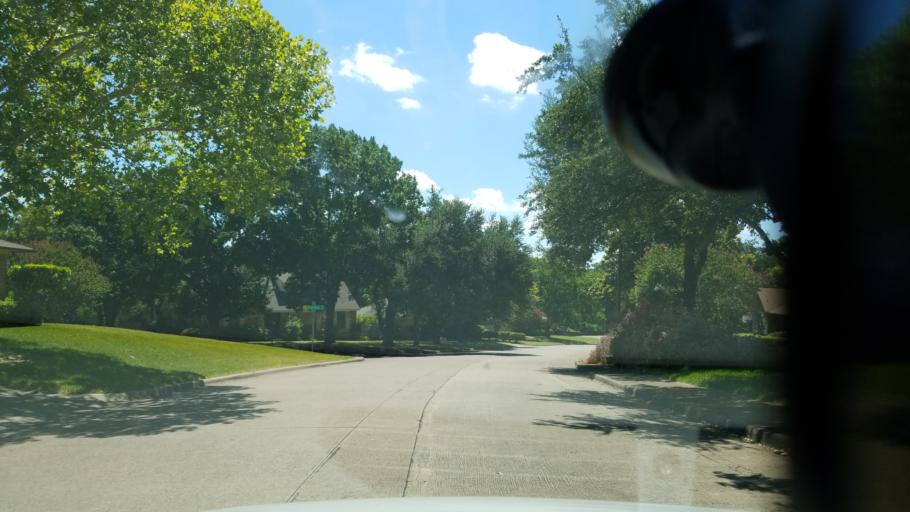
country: US
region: Texas
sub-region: Dallas County
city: Cockrell Hill
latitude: 32.6816
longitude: -96.8320
